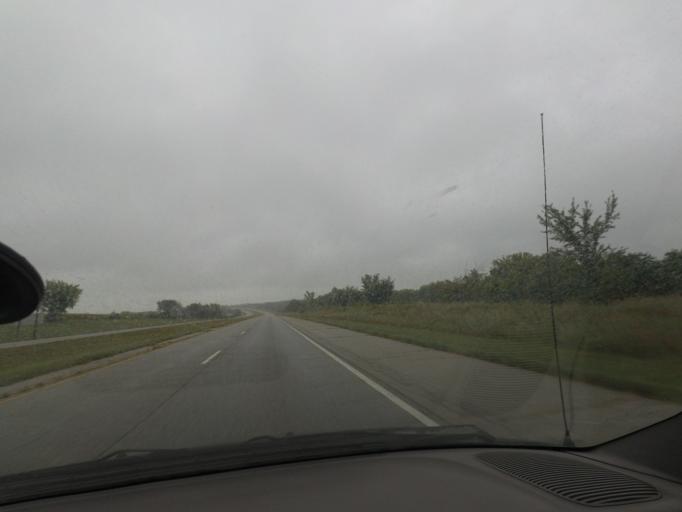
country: US
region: Illinois
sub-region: Pike County
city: Barry
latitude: 39.6947
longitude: -91.0043
